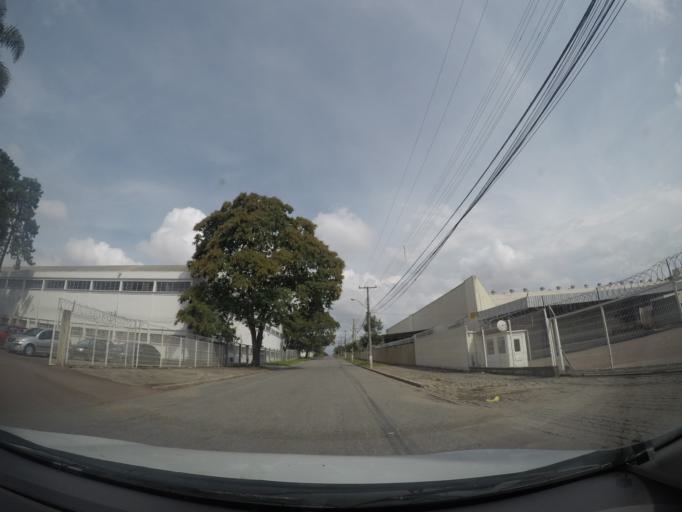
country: BR
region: Parana
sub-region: Curitiba
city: Curitiba
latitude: -25.4862
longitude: -49.2697
